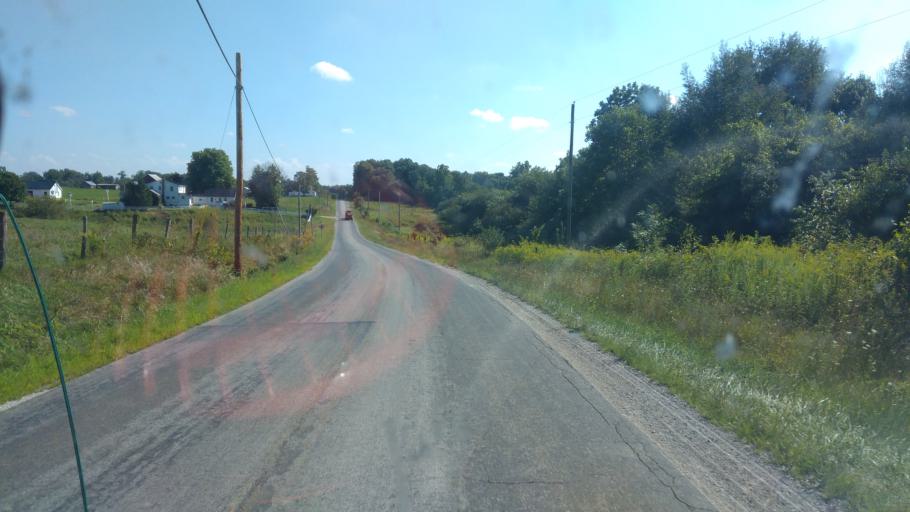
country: US
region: Ohio
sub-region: Ashland County
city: Ashland
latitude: 40.9096
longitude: -82.4359
